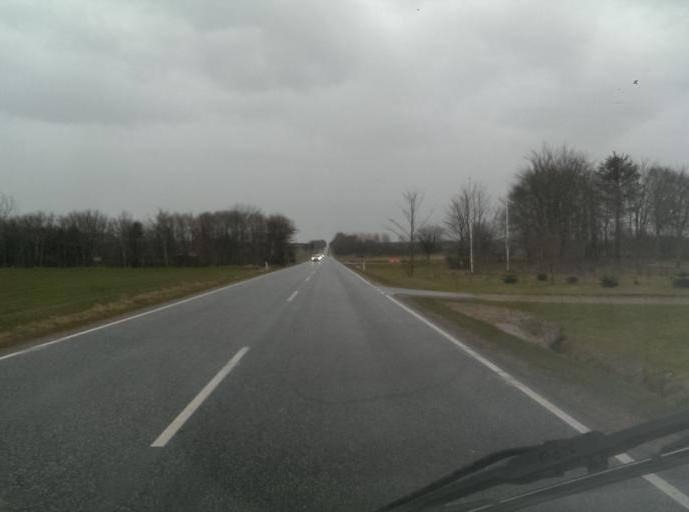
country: DK
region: Central Jutland
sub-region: Ringkobing-Skjern Kommune
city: Ringkobing
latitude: 56.0828
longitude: 8.4032
